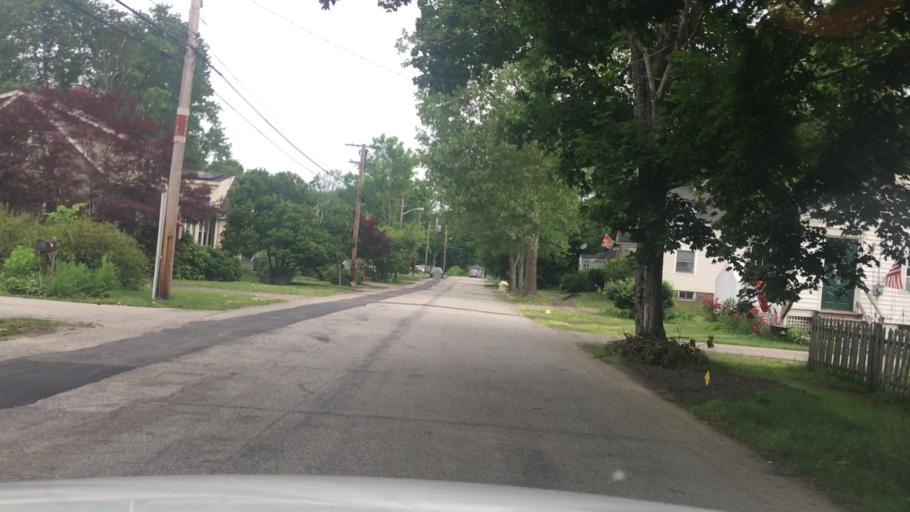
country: US
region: New Hampshire
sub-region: Rockingham County
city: Exeter
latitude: 42.9830
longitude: -70.9656
